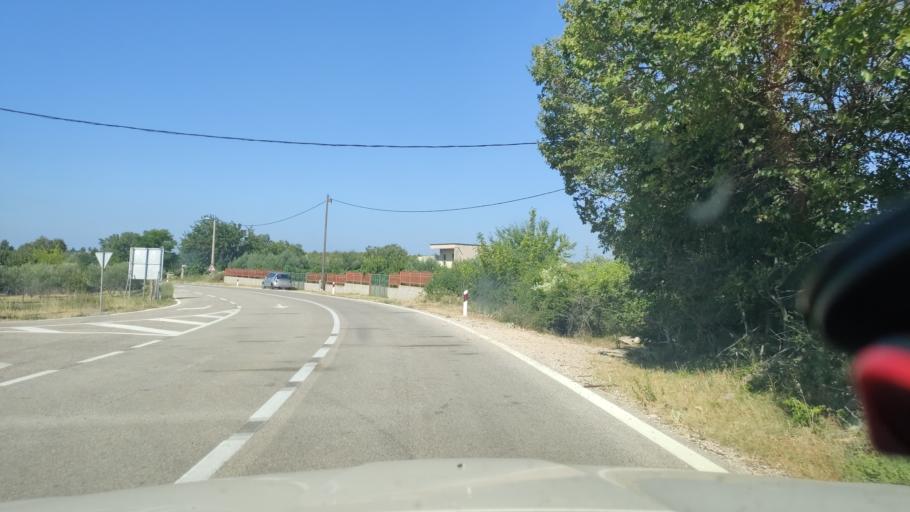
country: HR
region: Sibensko-Kniniska
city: Zaton
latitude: 43.9121
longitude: 15.8421
